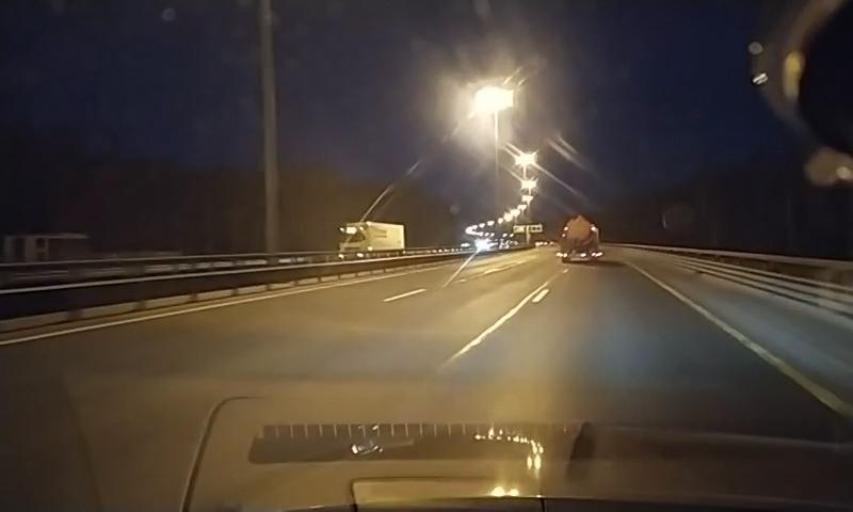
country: RU
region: St.-Petersburg
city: Pesochnyy
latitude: 60.0766
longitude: 30.1280
